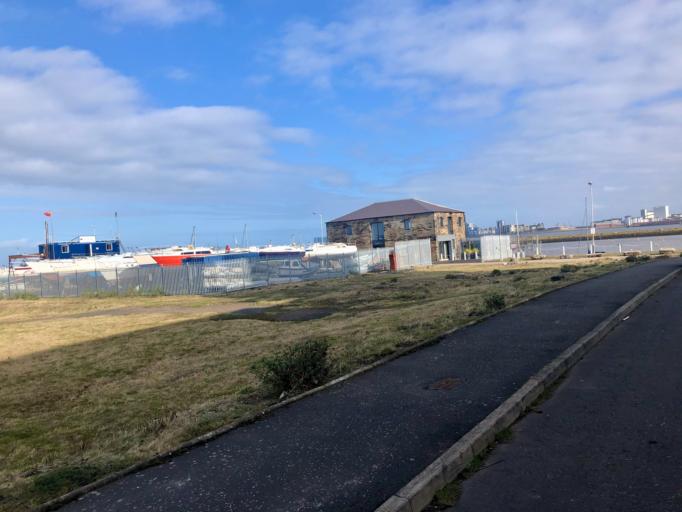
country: GB
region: Scotland
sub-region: Edinburgh
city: Edinburgh
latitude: 55.9841
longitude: -3.2240
